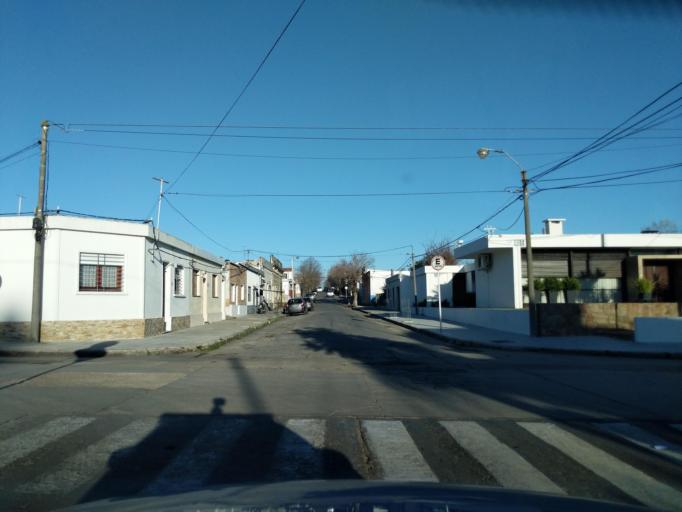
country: UY
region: Florida
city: Florida
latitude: -34.1003
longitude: -56.2211
